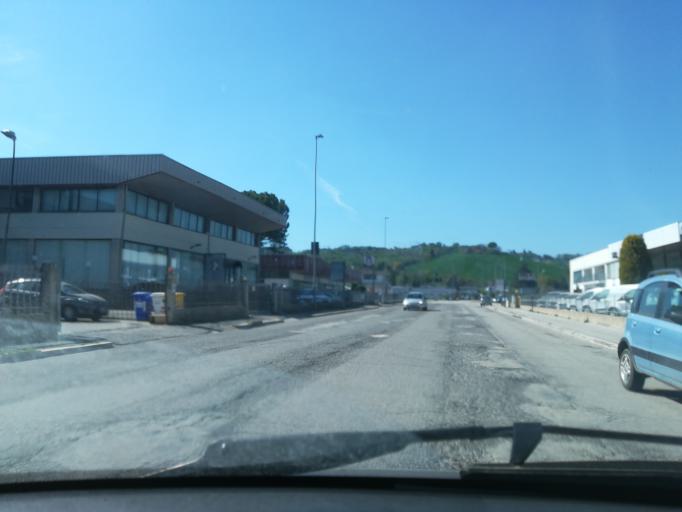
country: IT
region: The Marches
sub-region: Provincia di Macerata
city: Piediripa
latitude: 43.2800
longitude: 13.4899
